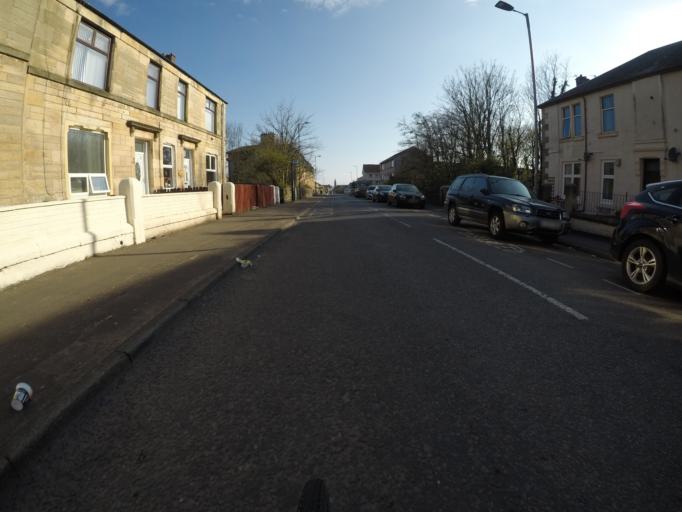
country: GB
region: Scotland
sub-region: North Ayrshire
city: Saltcoats
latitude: 55.6380
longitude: -4.7827
